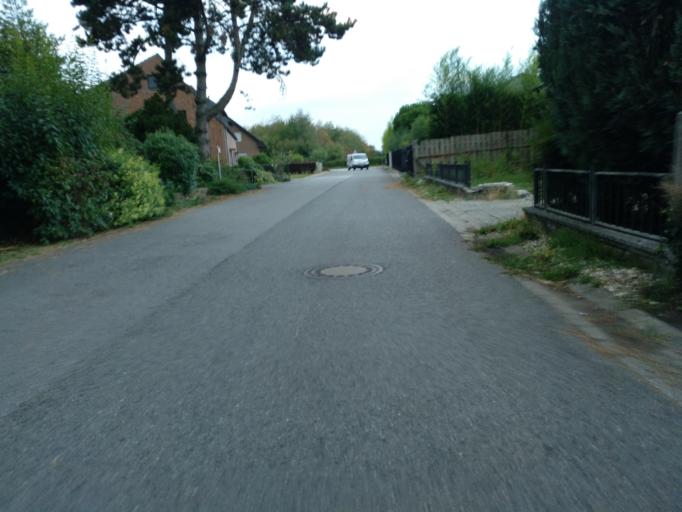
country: DE
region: North Rhine-Westphalia
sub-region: Regierungsbezirk Dusseldorf
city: Moers
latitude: 51.4150
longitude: 6.5782
